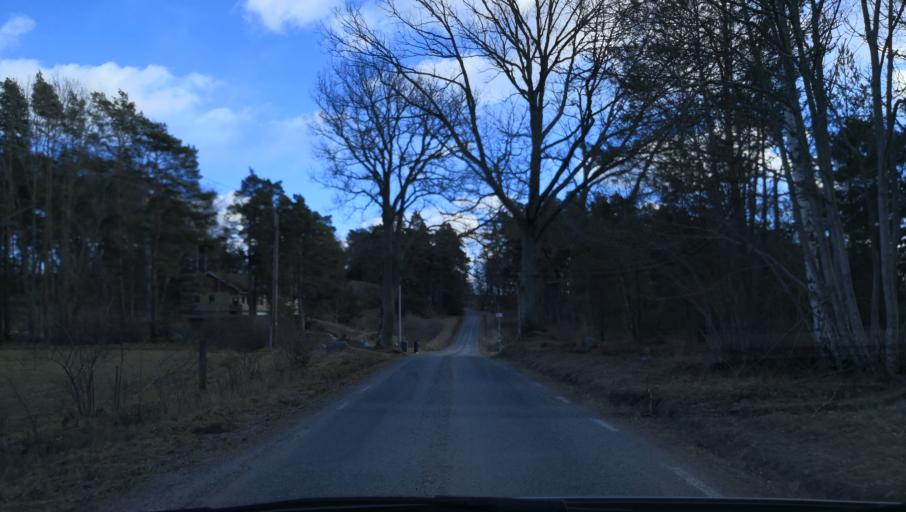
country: SE
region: Stockholm
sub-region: Varmdo Kommun
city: Mortnas
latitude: 59.3825
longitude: 18.4559
